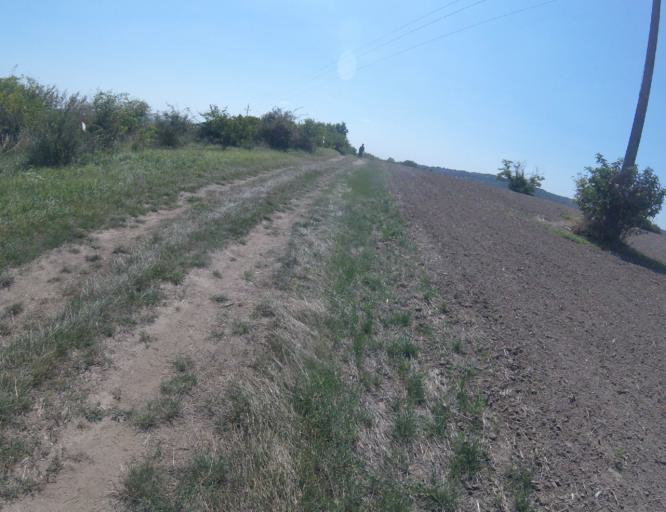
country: HU
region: Fejer
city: Velence
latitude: 47.2605
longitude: 18.6469
